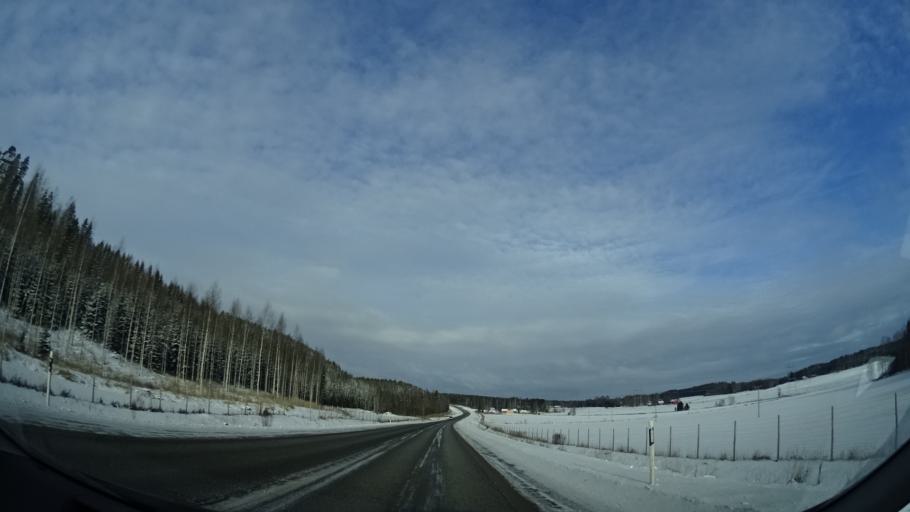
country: FI
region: Uusimaa
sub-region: Helsinki
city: Karkkila
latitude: 60.5801
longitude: 24.1337
